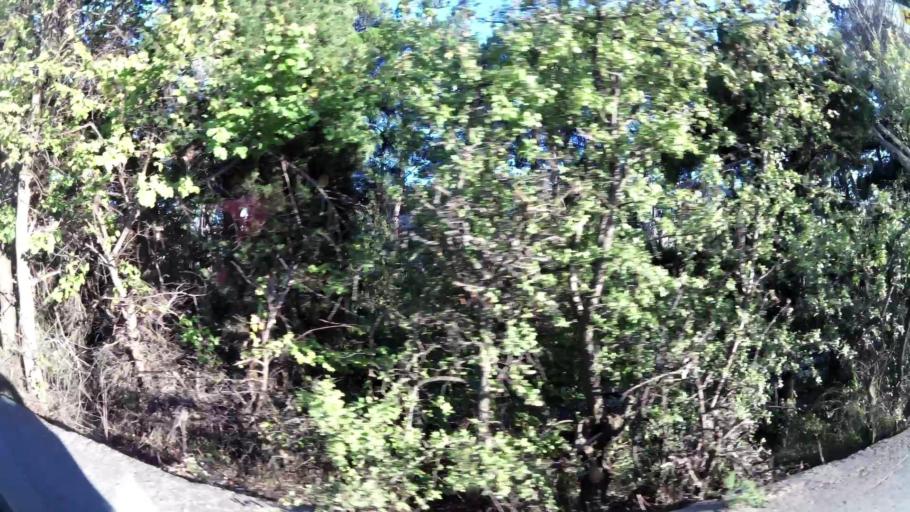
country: GR
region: Attica
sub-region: Nomarchia Anatolikis Attikis
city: Anoixi
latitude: 38.1342
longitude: 23.8552
